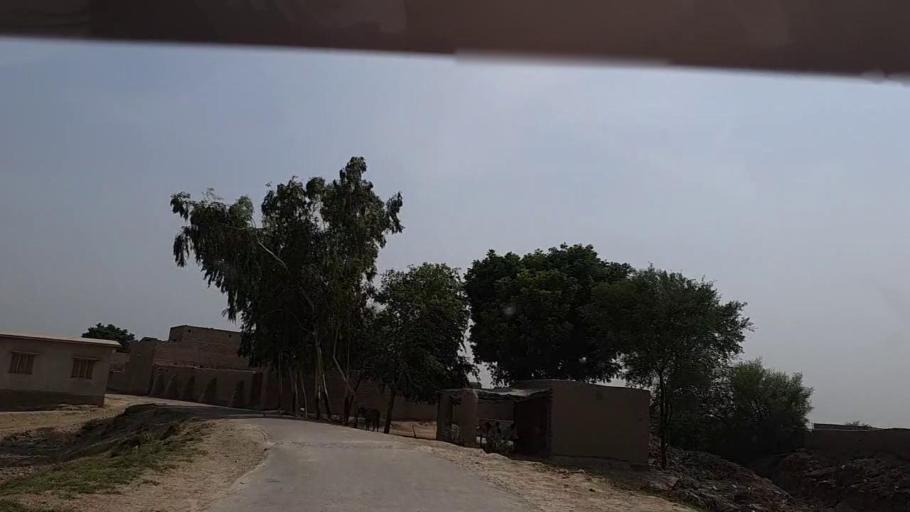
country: PK
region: Sindh
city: Khairpur Nathan Shah
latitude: 27.0614
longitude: 67.6862
